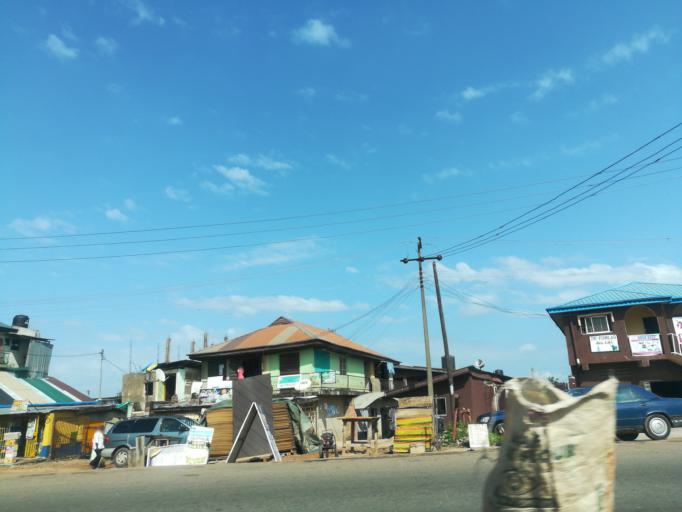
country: NG
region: Oyo
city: Ibadan
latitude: 7.4082
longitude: 3.9464
